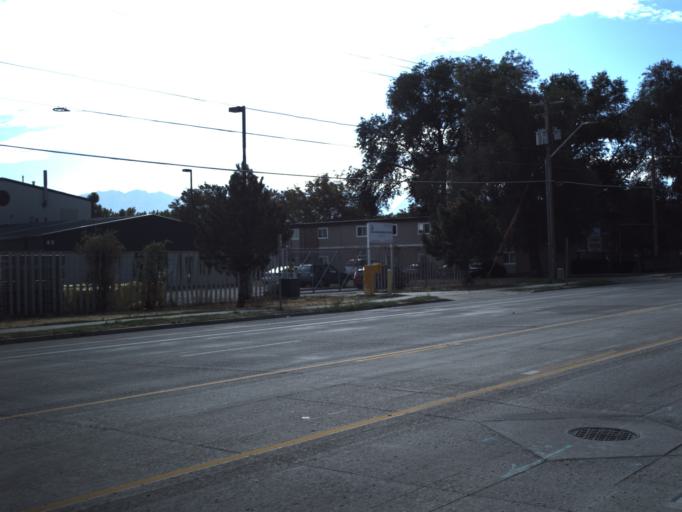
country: US
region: Utah
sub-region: Salt Lake County
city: Salt Lake City
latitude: 40.7746
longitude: -111.9394
